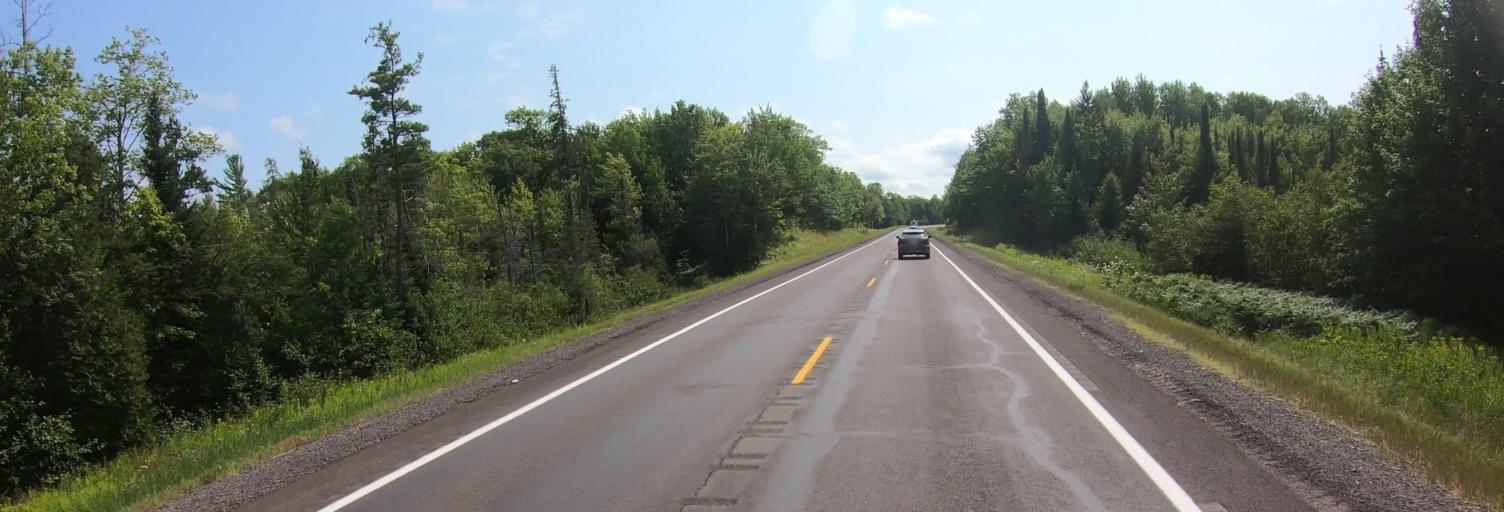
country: US
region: Michigan
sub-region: Houghton County
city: Hancock
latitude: 46.8761
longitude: -88.8709
